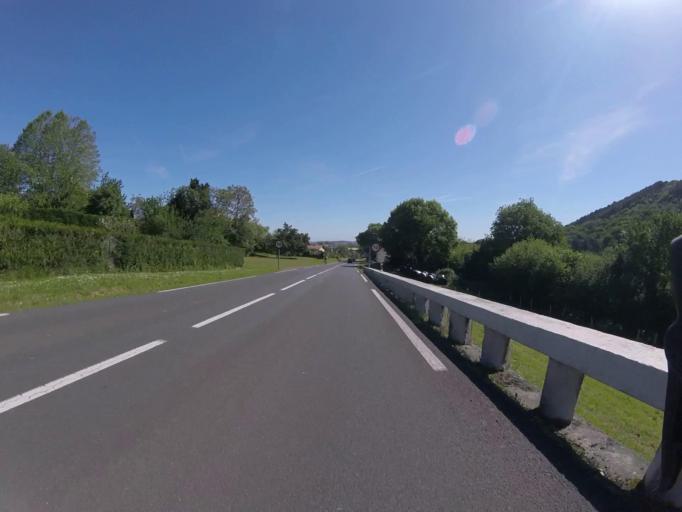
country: ES
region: Basque Country
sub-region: Provincia de Guipuzcoa
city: Irun
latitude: 43.3230
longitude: -1.8262
